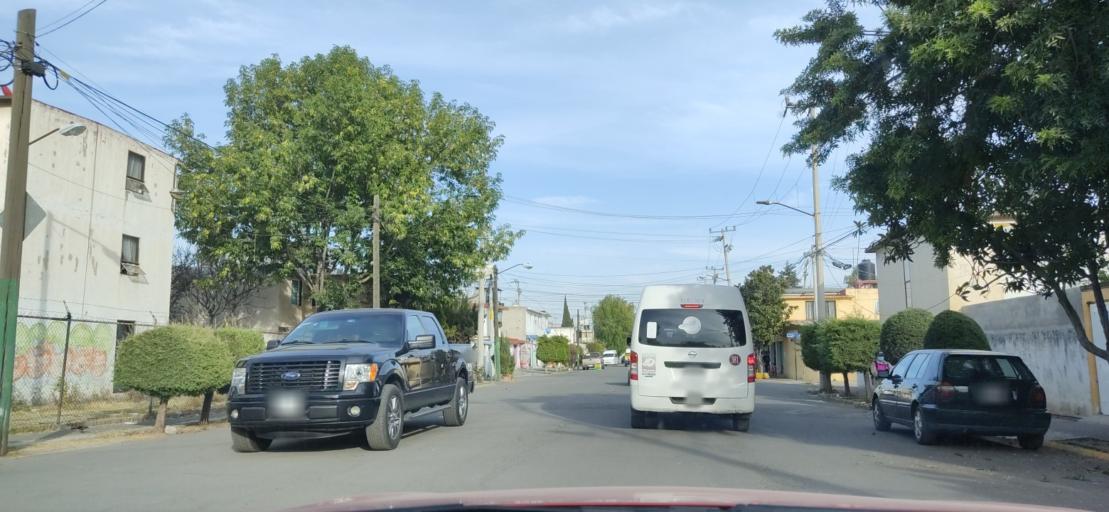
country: MX
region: Mexico
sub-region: Cuautitlan
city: San Jose del Puente
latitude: 19.6921
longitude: -99.2070
